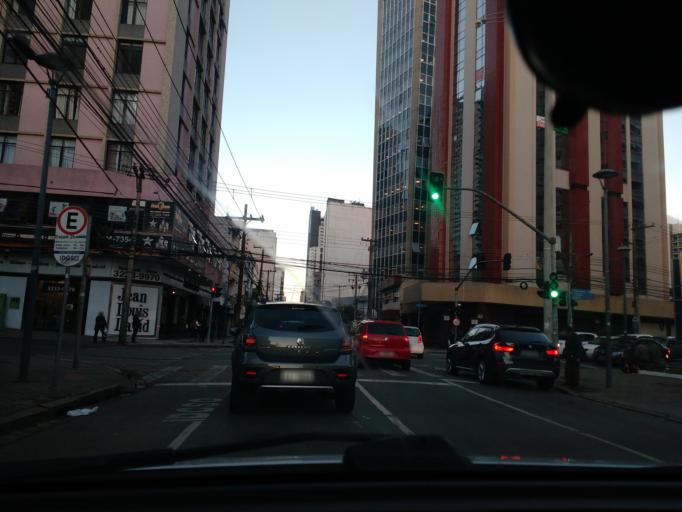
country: BR
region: Parana
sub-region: Curitiba
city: Curitiba
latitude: -25.4351
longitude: -49.2818
